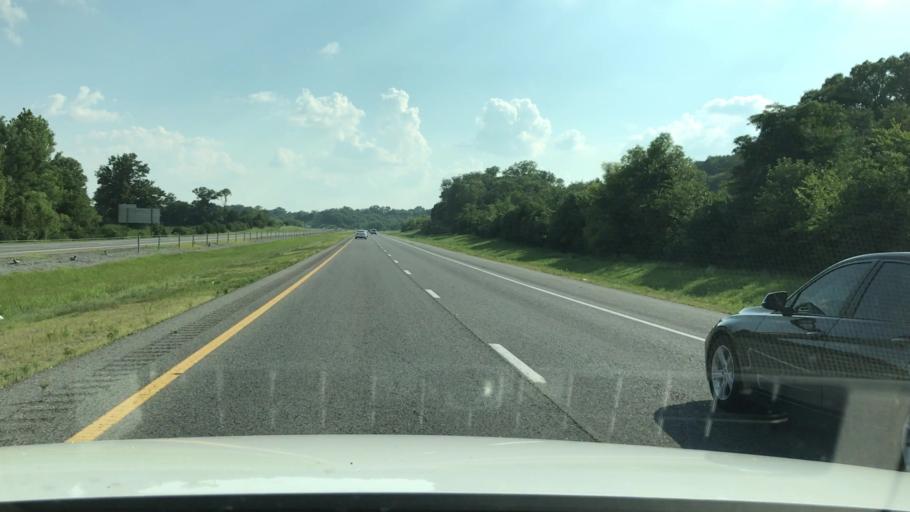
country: US
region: Tennessee
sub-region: Sumner County
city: Shackle Island
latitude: 36.3509
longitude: -86.5429
